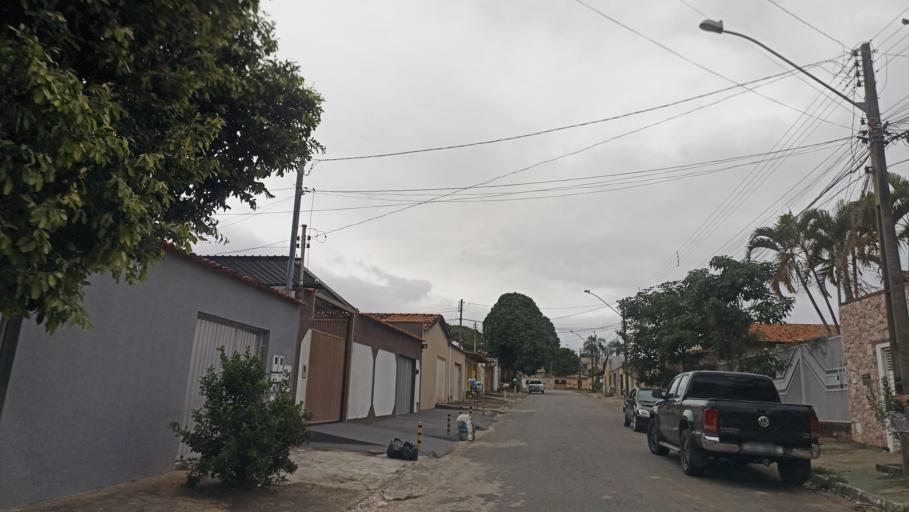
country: BR
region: Goias
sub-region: Goiania
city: Goiania
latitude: -16.6856
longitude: -49.3374
